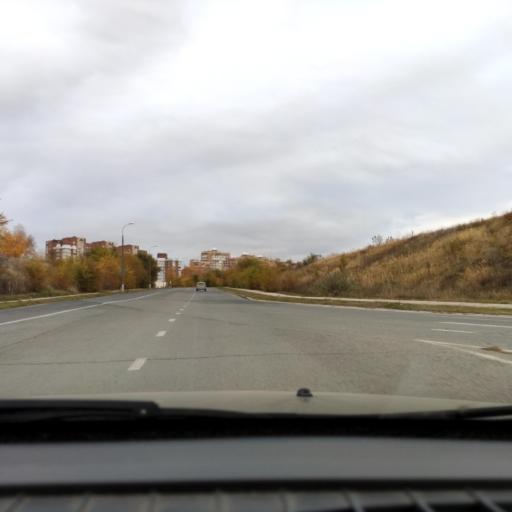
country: RU
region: Samara
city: Tol'yatti
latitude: 53.4979
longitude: 49.2713
